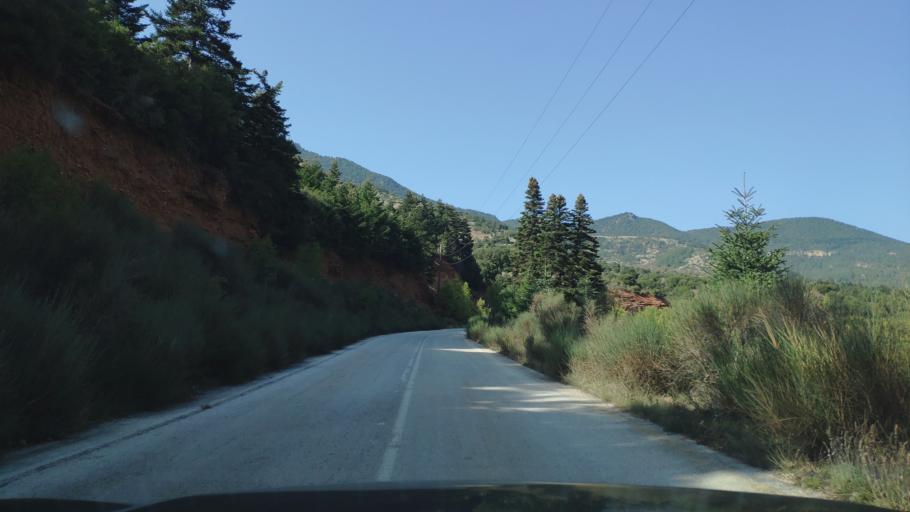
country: GR
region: West Greece
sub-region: Nomos Achaias
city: Aiyira
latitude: 37.9781
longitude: 22.3541
